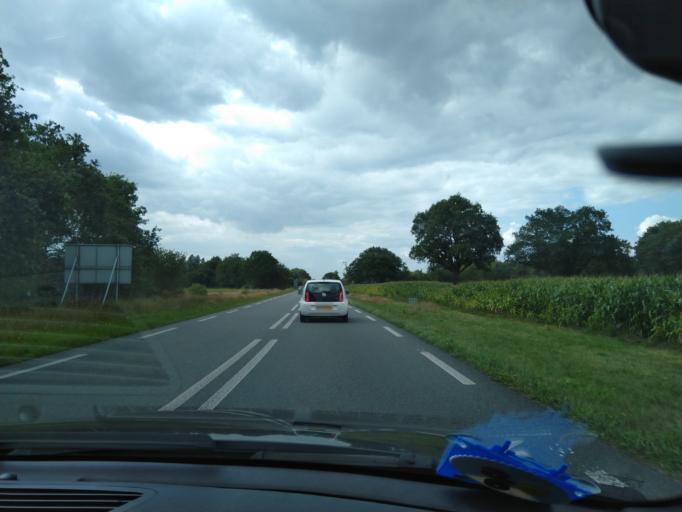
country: NL
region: Drenthe
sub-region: Gemeente Tynaarlo
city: Vries
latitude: 53.1387
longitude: 6.4935
